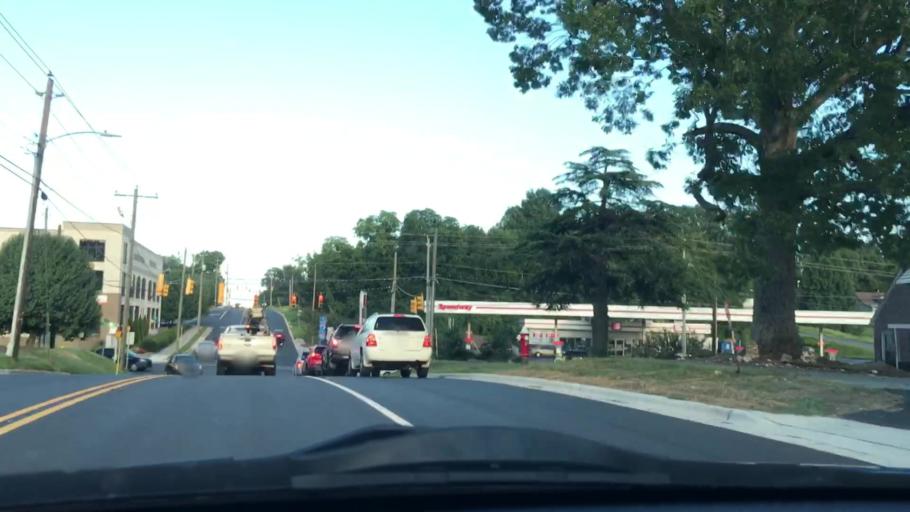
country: US
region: North Carolina
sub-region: Randolph County
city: Asheboro
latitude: 35.7146
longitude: -79.8137
